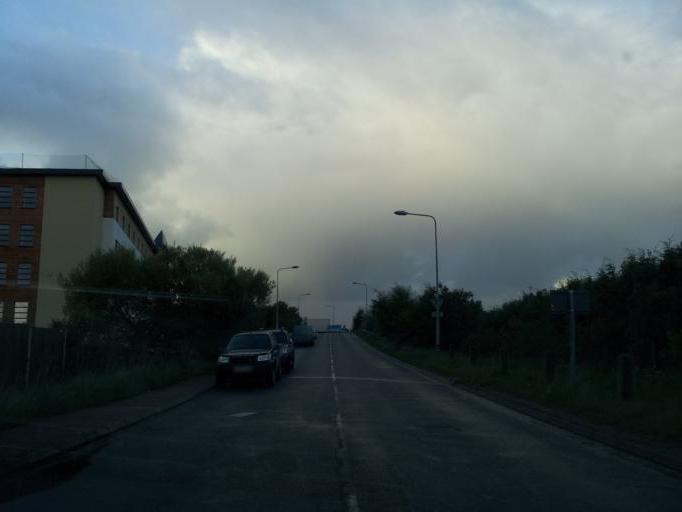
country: GB
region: England
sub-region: Norfolk
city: Great Yarmouth
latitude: 52.6164
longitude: 1.7212
